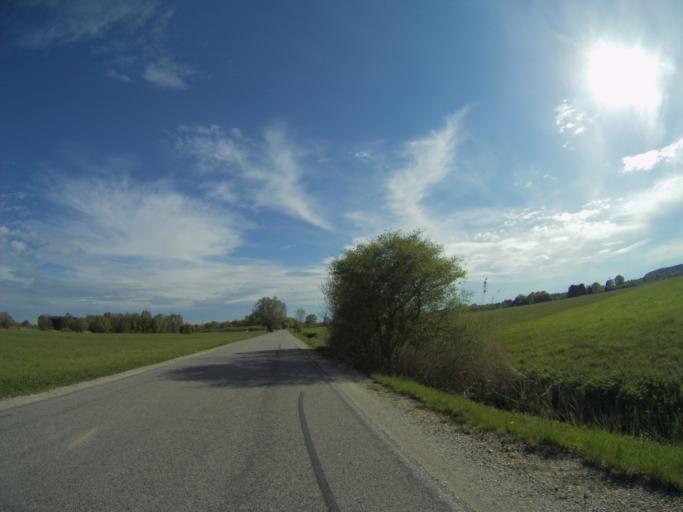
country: DE
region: Bavaria
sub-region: Upper Bavaria
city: Freising
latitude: 48.3829
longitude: 11.6993
